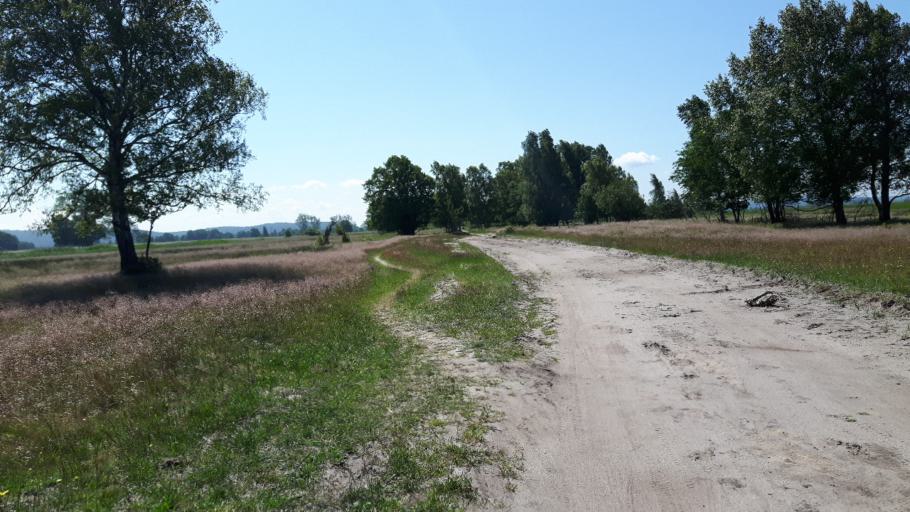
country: PL
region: Pomeranian Voivodeship
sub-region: Powiat slupski
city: Smoldzino
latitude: 54.6716
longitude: 17.1592
